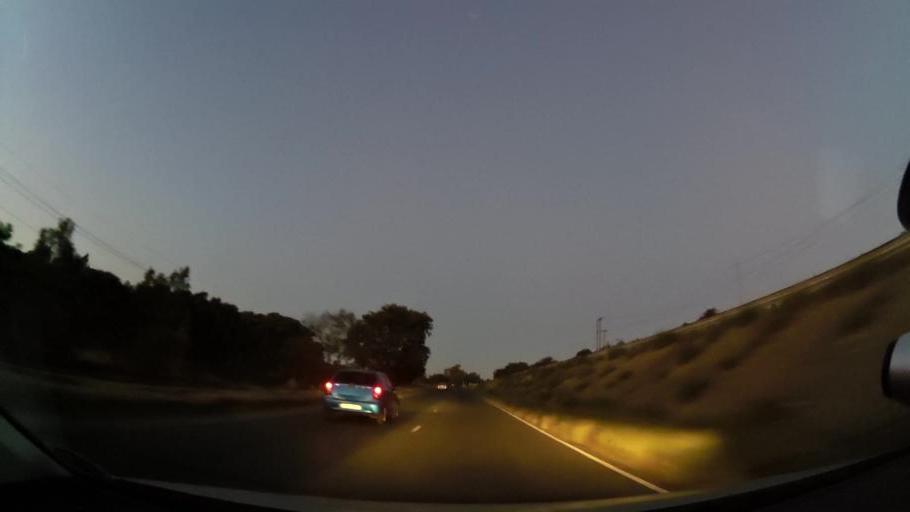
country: ZA
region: Gauteng
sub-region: City of Tshwane Metropolitan Municipality
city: Pretoria
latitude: -25.7744
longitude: 28.1566
